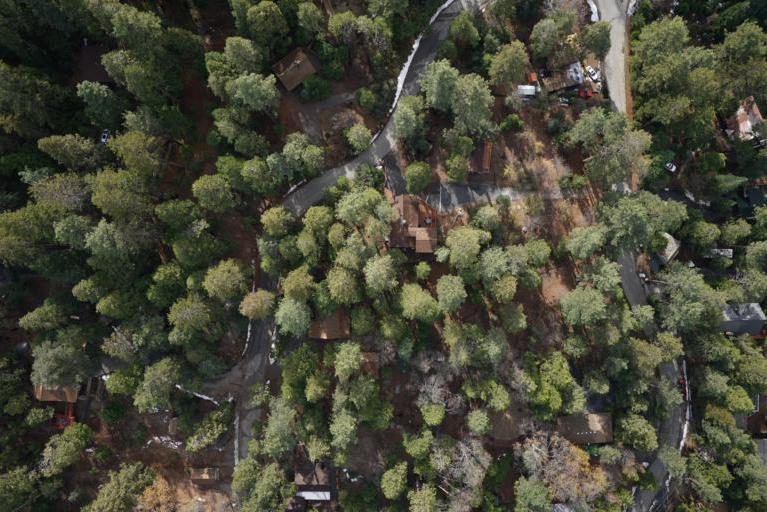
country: US
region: California
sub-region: Riverside County
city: Idyllwild
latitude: 33.7441
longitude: -116.7019
